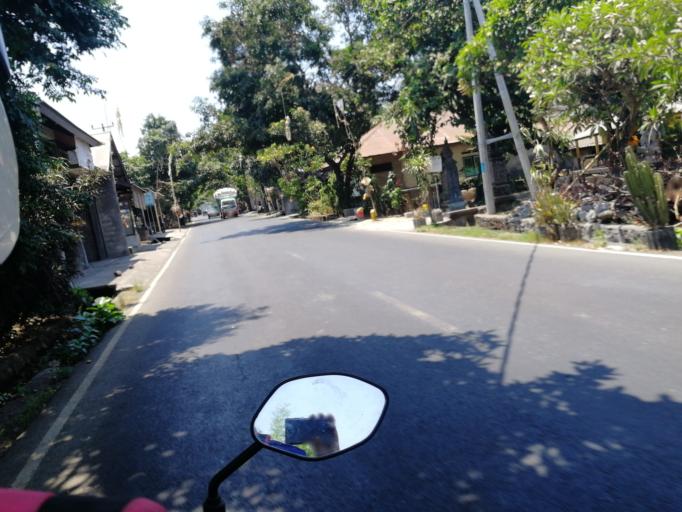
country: ID
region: Bali
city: Banjar Trunyan
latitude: -8.1472
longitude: 115.4036
